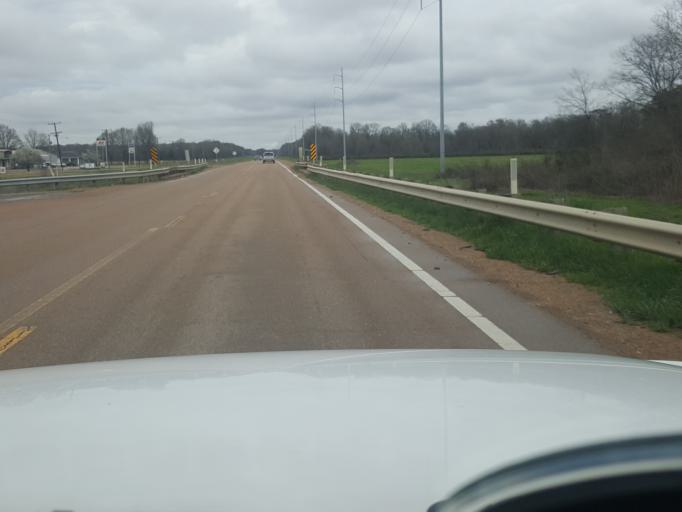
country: US
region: Mississippi
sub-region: Yazoo County
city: Yazoo City
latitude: 32.8612
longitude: -90.4275
